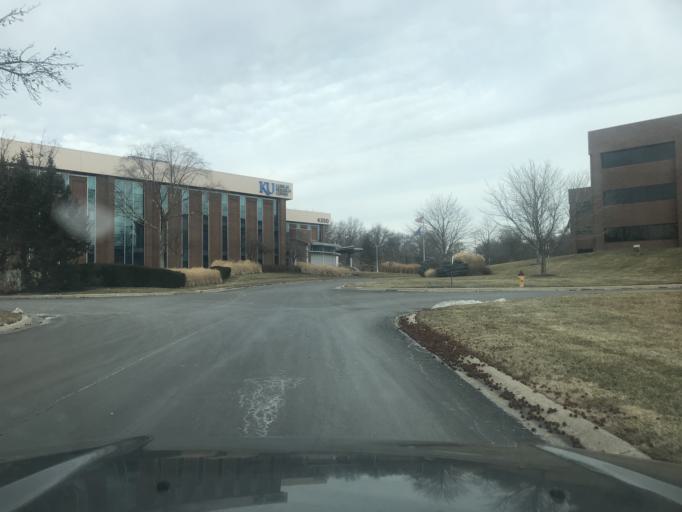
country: US
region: Kansas
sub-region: Johnson County
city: Fairway
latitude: 39.0276
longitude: -94.6363
